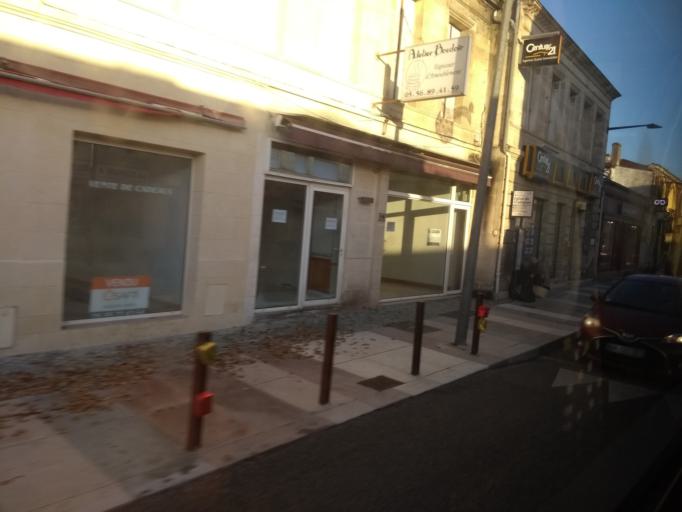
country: FR
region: Aquitaine
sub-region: Departement de la Gironde
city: Gradignan
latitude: 44.7722
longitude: -0.6144
